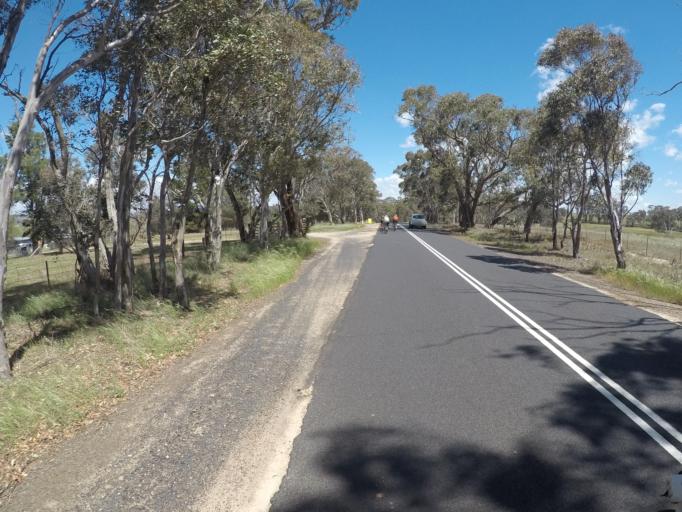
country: AU
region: New South Wales
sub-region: Bathurst Regional
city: Perthville
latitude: -33.5347
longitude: 149.4428
